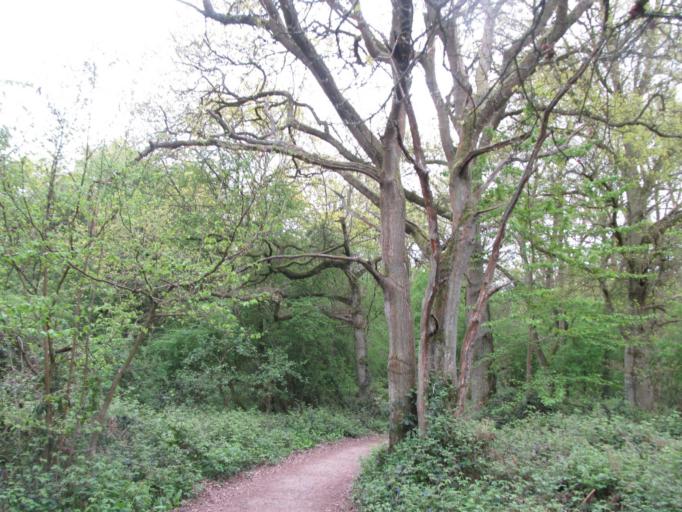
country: GB
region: England
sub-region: Royal Borough of Windsor and Maidenhead
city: Bisham
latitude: 51.5457
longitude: -0.7569
